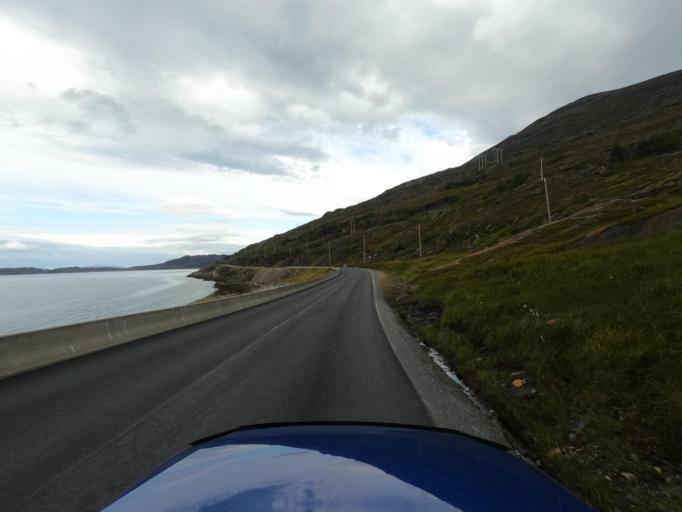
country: NO
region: Finnmark Fylke
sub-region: Hammerfest
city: Rypefjord
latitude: 70.5690
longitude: 23.6970
